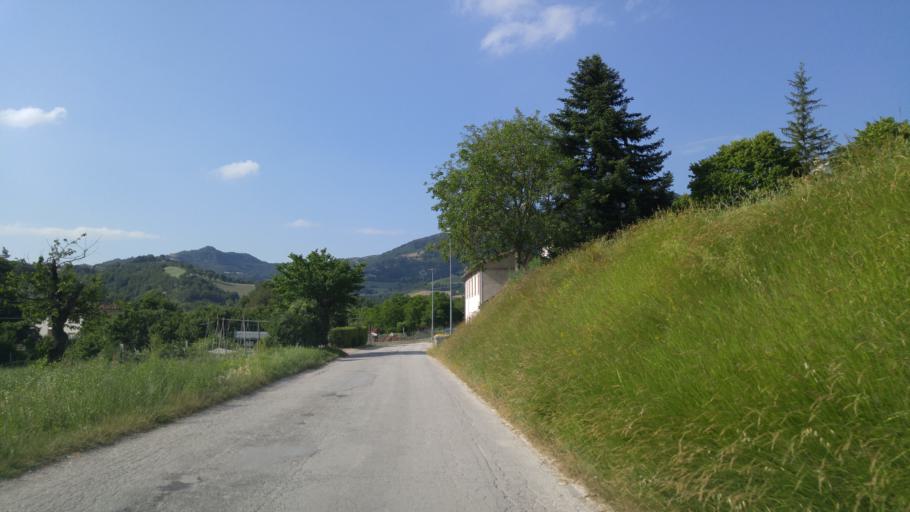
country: IT
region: The Marches
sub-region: Provincia di Pesaro e Urbino
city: Acqualagna
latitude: 43.6269
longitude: 12.6860
